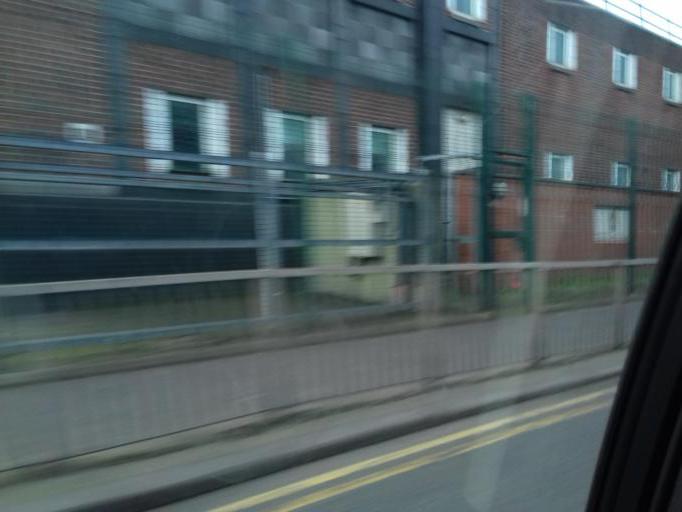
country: GB
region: Northern Ireland
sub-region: City of Belfast
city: Belfast
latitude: 54.6162
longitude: -5.9244
